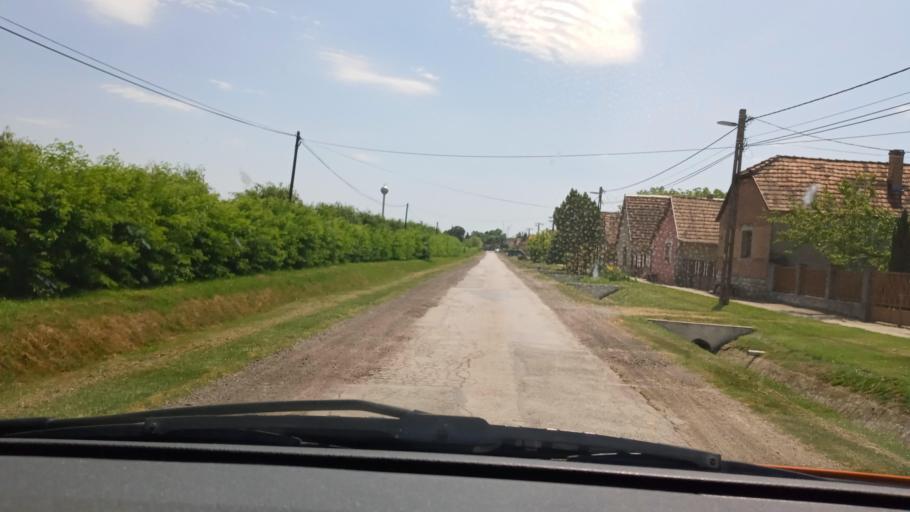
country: HU
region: Baranya
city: Harkany
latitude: 45.8331
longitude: 18.1365
